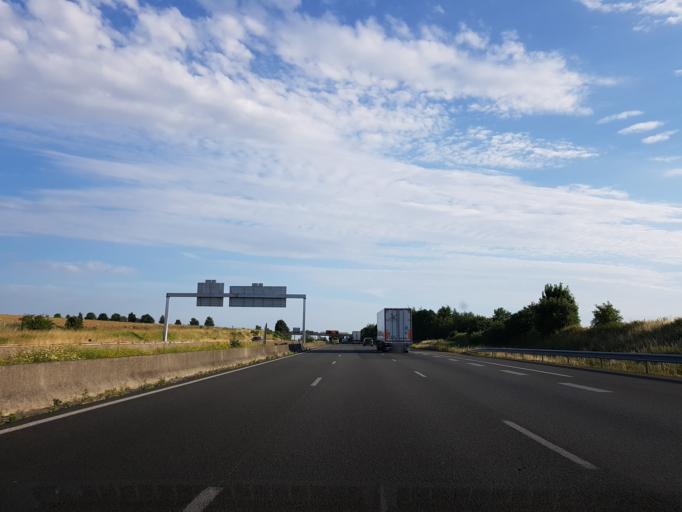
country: FR
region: Picardie
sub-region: Departement de la Somme
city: Moislains
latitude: 50.0103
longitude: 2.8775
